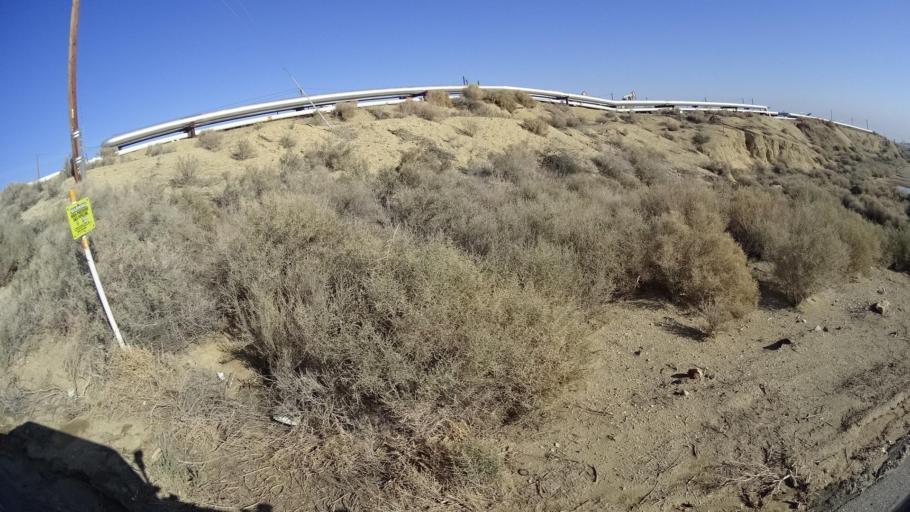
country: US
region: California
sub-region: Kern County
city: Taft Heights
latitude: 35.2242
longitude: -119.6228
